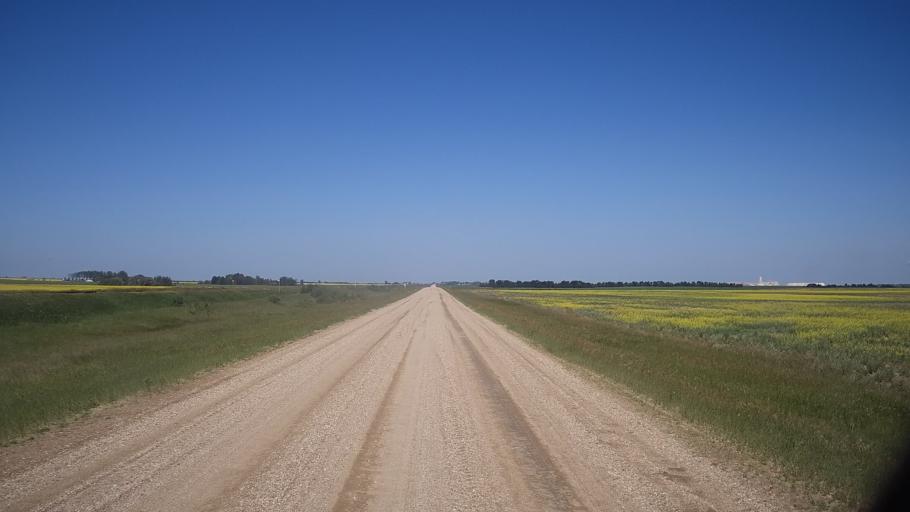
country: CA
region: Saskatchewan
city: Watrous
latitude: 51.8725
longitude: -105.9980
